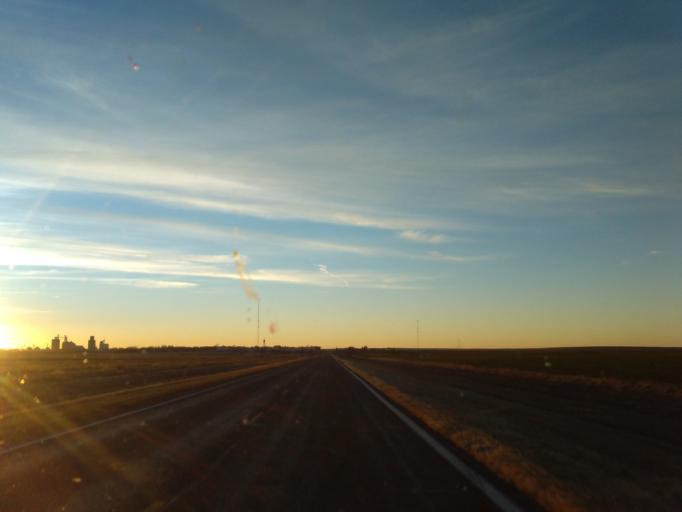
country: US
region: Kansas
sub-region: Wallace County
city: Sharon Springs
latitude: 38.9020
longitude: -101.7250
